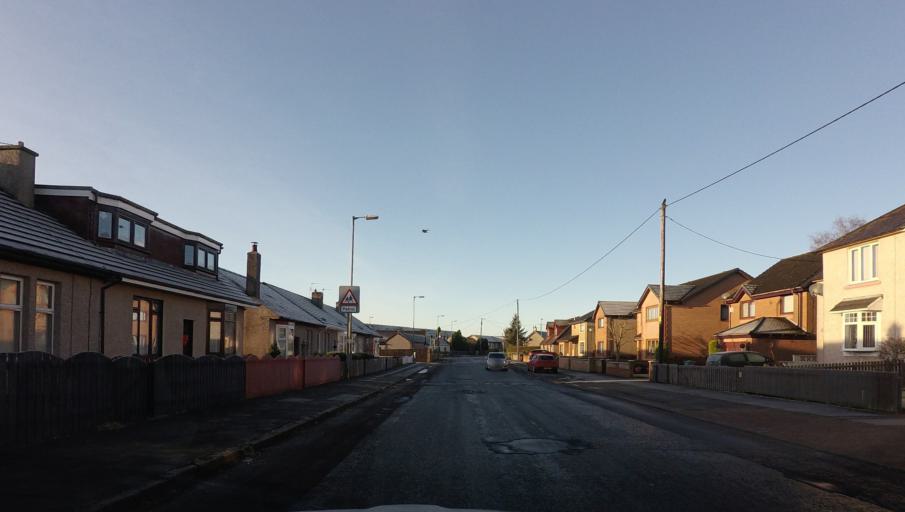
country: GB
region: Scotland
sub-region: North Lanarkshire
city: Shotts
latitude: 55.8237
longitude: -3.8076
